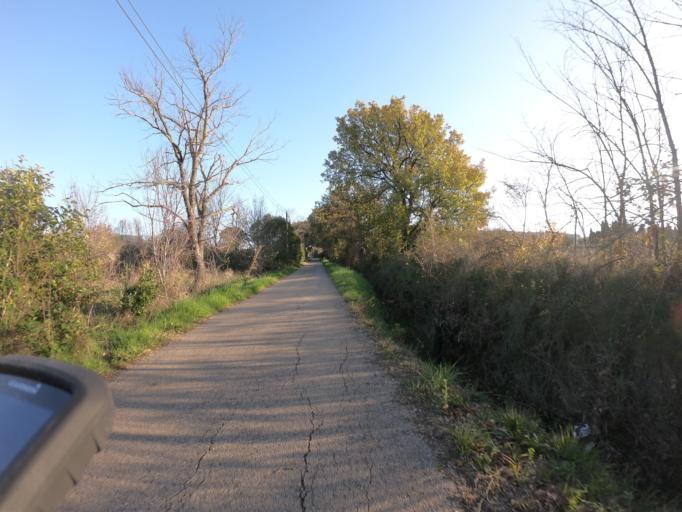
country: FR
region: Provence-Alpes-Cote d'Azur
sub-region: Departement du Var
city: Le Pradet
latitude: 43.1148
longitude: 6.0361
